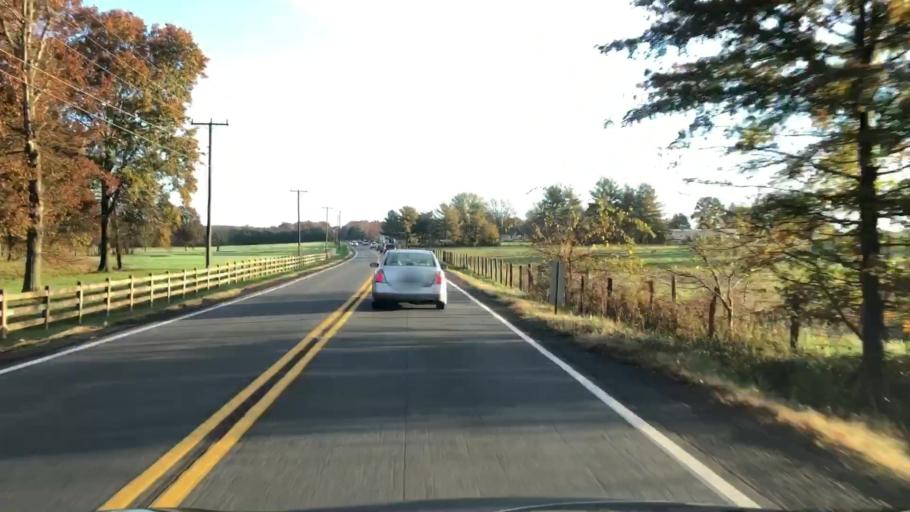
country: US
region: Virginia
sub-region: Fauquier County
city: Bealeton
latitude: 38.5880
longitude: -77.7581
